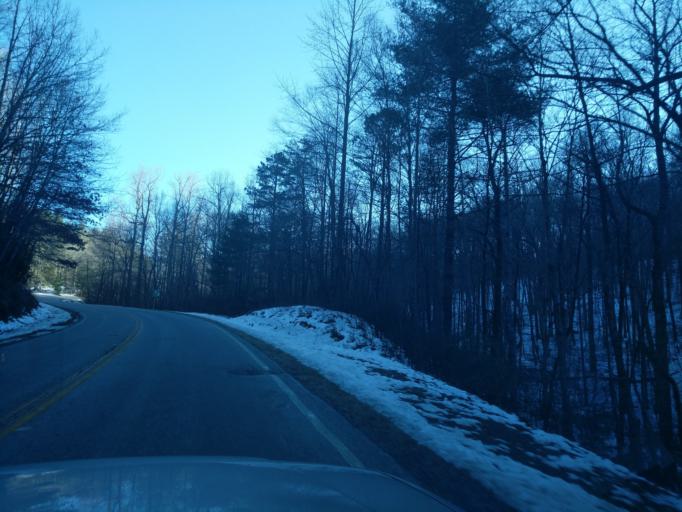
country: US
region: Georgia
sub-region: Towns County
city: Hiawassee
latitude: 34.9141
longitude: -83.6214
